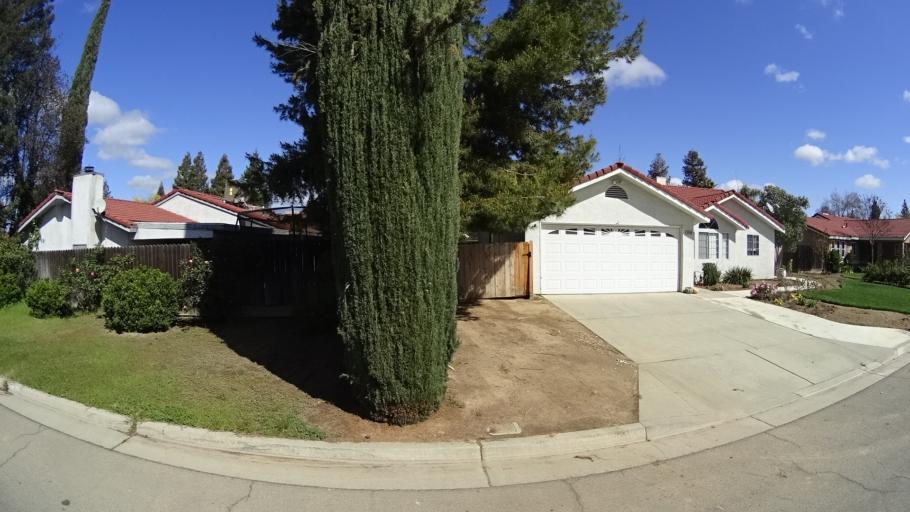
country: US
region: California
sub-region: Fresno County
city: West Park
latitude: 36.8235
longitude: -119.8919
